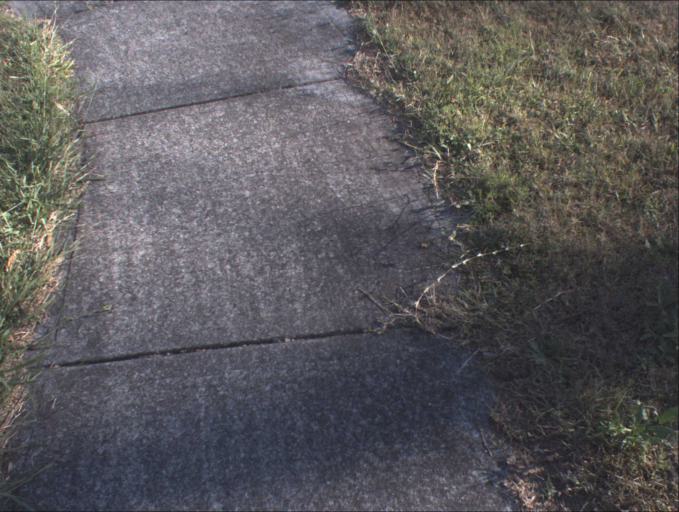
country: AU
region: Queensland
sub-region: Logan
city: Windaroo
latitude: -27.7263
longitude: 153.1917
